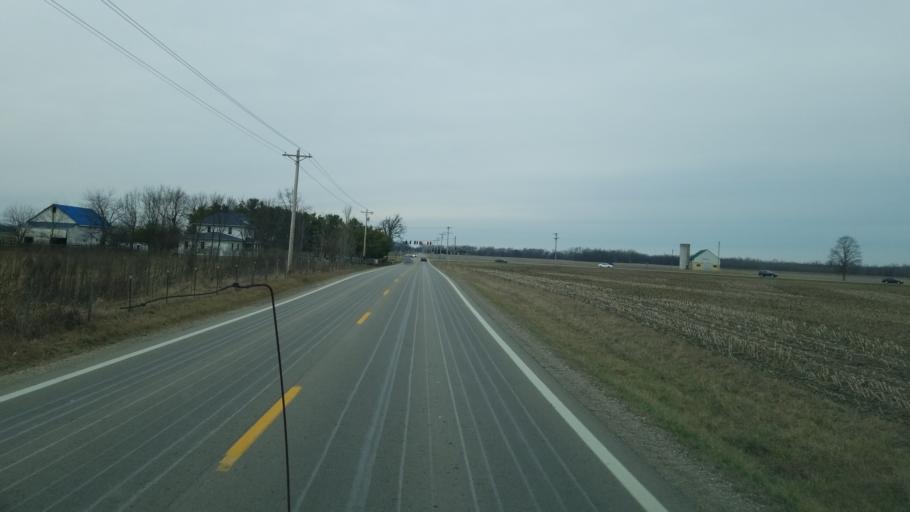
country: US
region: Ohio
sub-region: Pickaway County
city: Circleville
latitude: 39.6093
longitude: -83.0056
